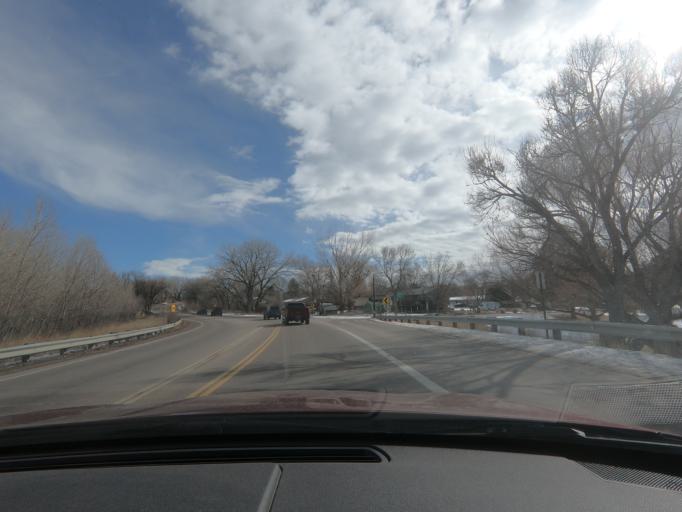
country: US
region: Colorado
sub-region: El Paso County
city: Security-Widefield
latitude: 38.7367
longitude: -104.7102
